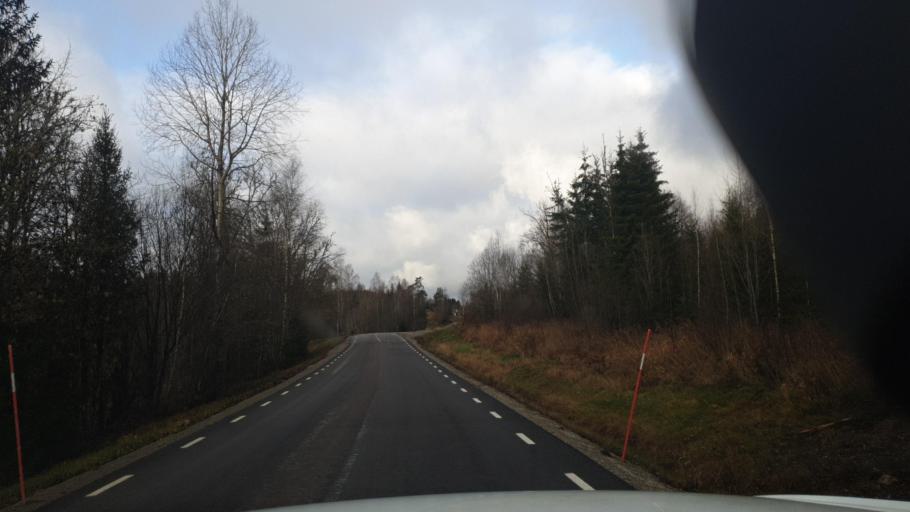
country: SE
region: Vaermland
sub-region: Sunne Kommun
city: Sunne
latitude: 59.6780
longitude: 12.8995
